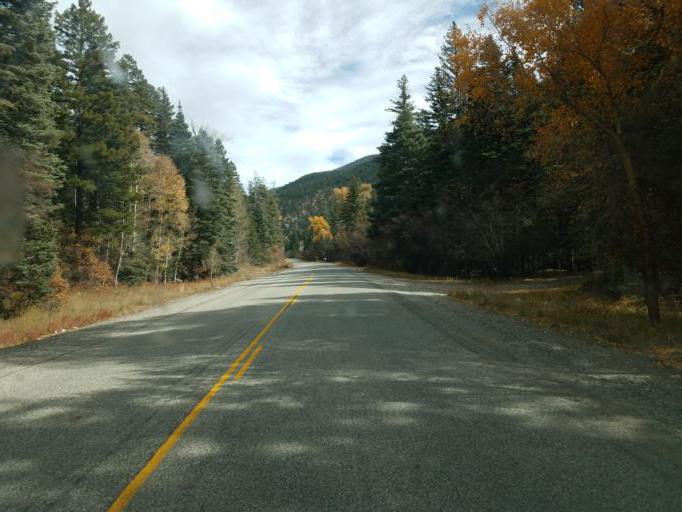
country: US
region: New Mexico
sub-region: Taos County
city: Arroyo Seco
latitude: 36.5489
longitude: -105.5491
